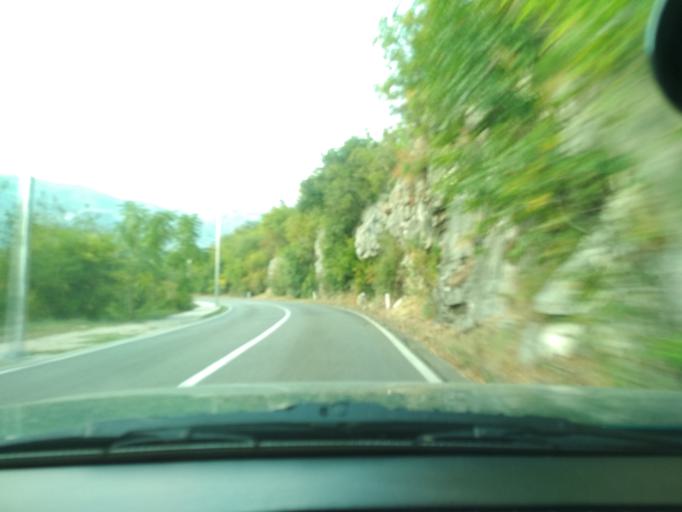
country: ME
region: Kotor
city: Risan
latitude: 42.4940
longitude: 18.6916
